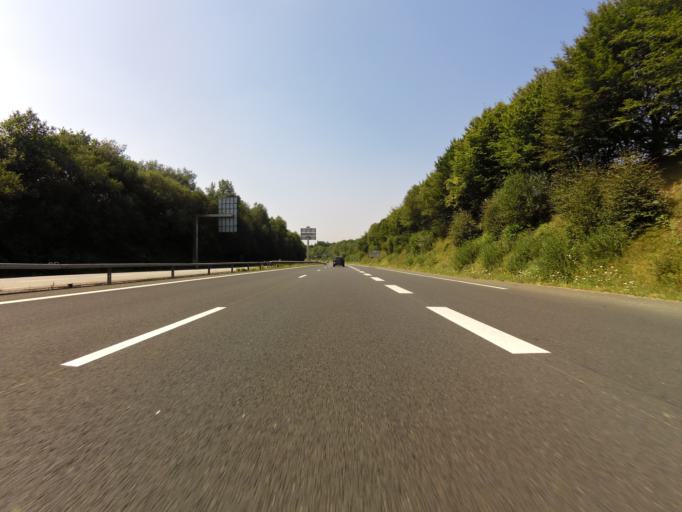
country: FR
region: Brittany
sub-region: Departement du Finistere
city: Pluguffan
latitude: 47.9558
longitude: -4.1725
